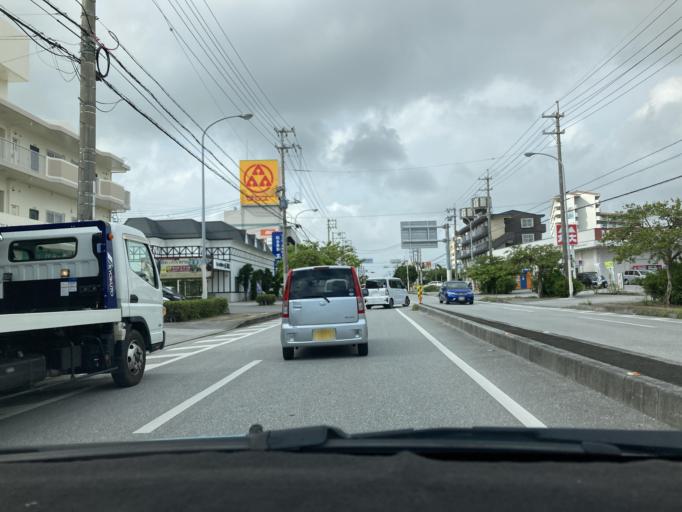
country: JP
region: Okinawa
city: Itoman
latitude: 26.1525
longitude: 127.6719
